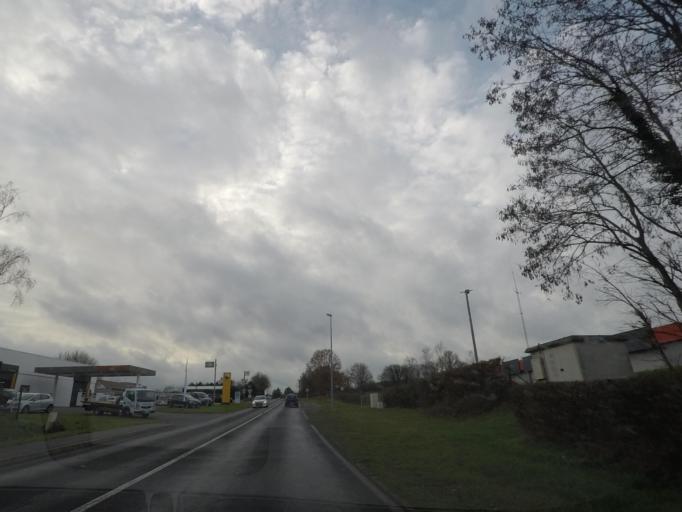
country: FR
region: Pays de la Loire
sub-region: Departement de la Sarthe
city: Vibraye
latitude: 48.0592
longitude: 0.7286
